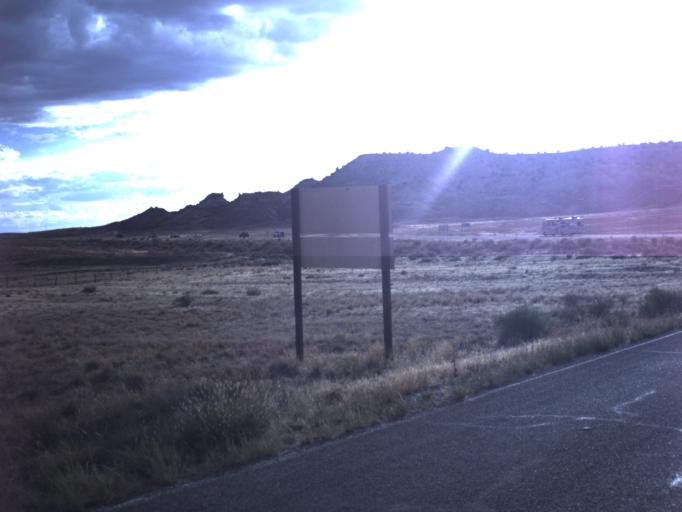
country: US
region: Utah
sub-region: San Juan County
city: Blanding
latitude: 37.4231
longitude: -109.4727
